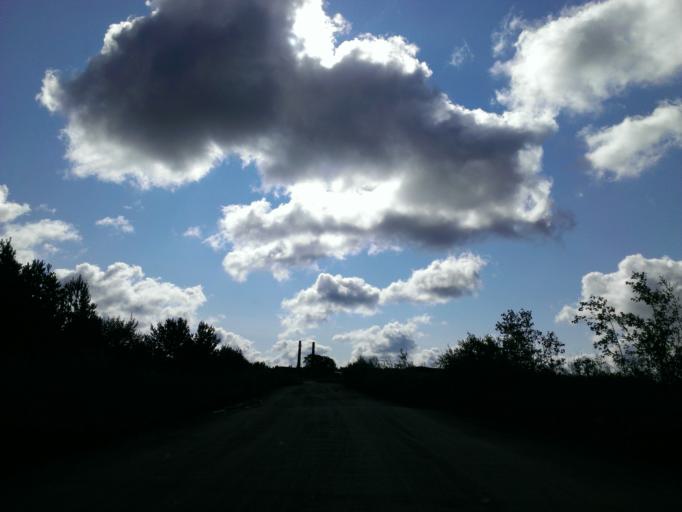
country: LV
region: Incukalns
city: Vangazi
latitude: 57.0916
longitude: 24.5081
